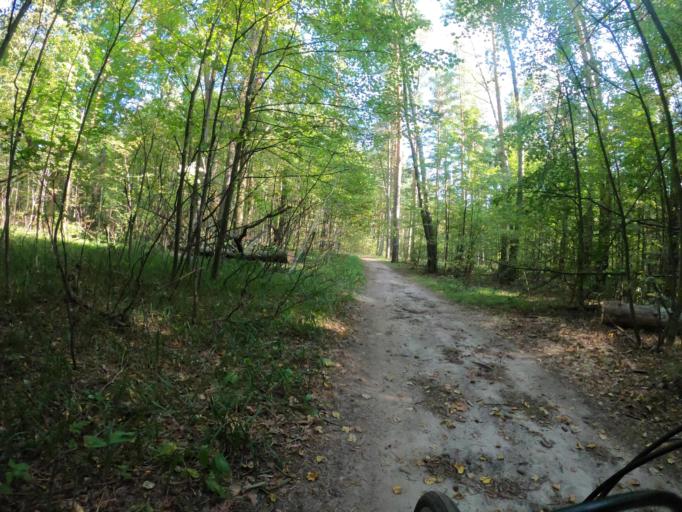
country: RU
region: Moskovskaya
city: Stupino
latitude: 54.8720
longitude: 38.0982
